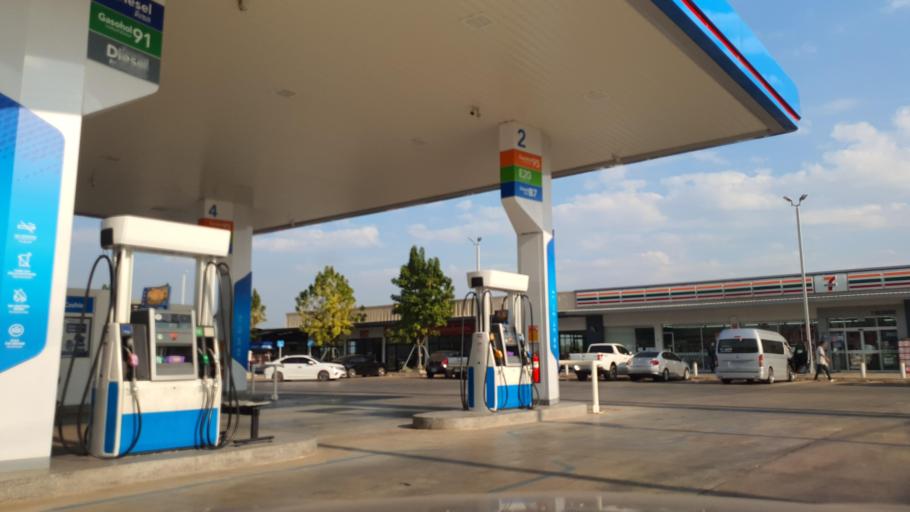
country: TH
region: Nakhon Phanom
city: Ban Phaeng
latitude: 18.0270
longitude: 104.1448
